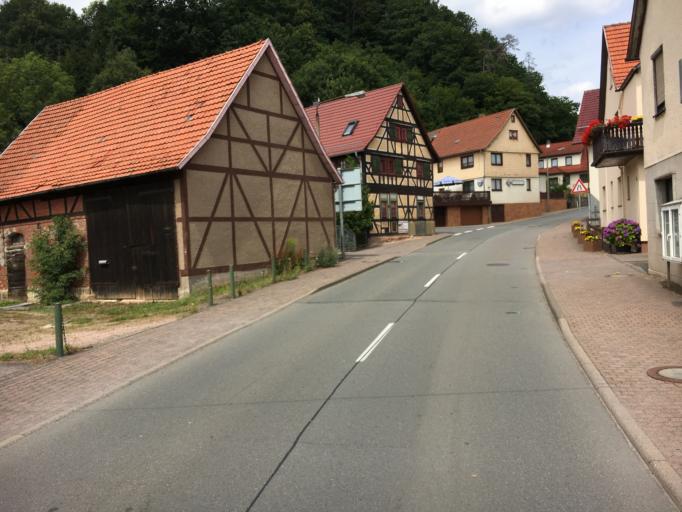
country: DE
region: Thuringia
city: Trusetal
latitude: 50.7874
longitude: 10.4081
